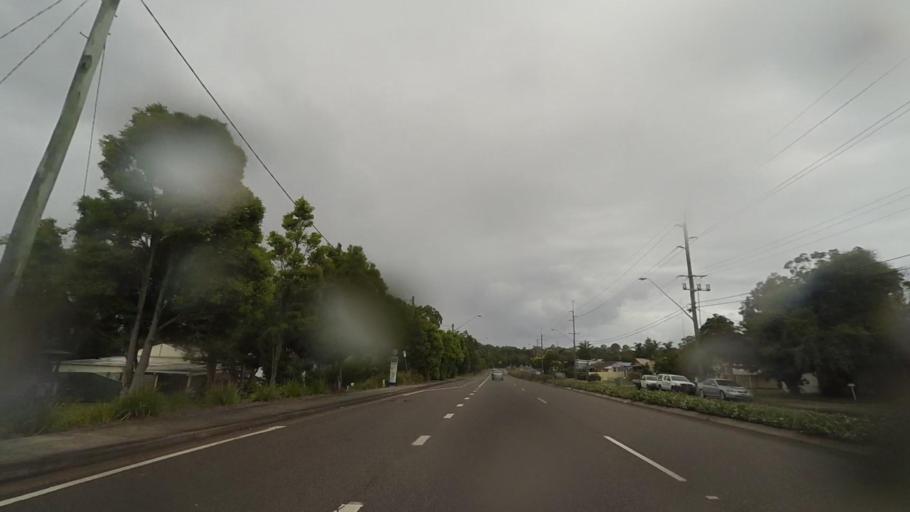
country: AU
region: New South Wales
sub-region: Wyong Shire
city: Tumbi Vmbi
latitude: -33.3629
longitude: 151.4492
